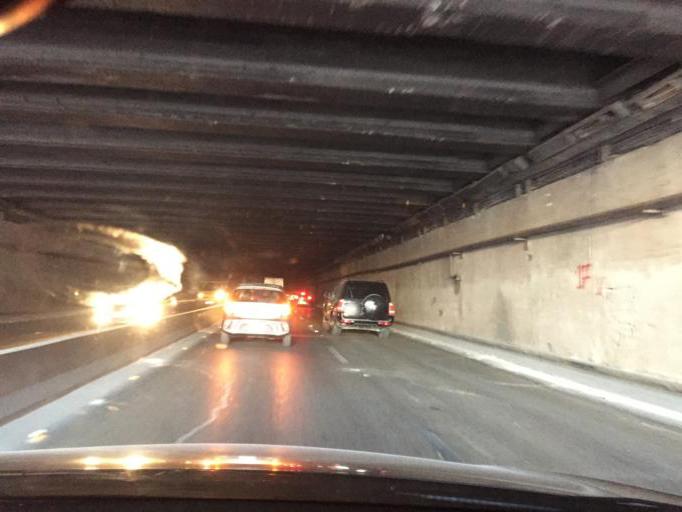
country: LB
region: Beyrouth
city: Beirut
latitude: 33.8874
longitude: 35.4989
